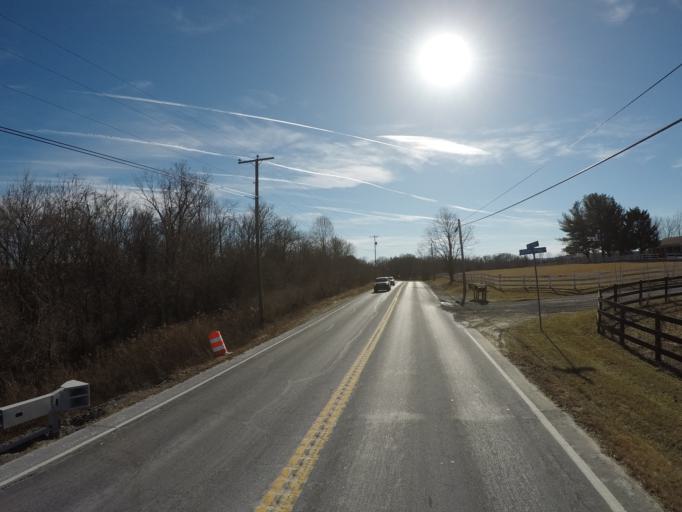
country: US
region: Maryland
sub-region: Frederick County
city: Point of Rocks
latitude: 39.2378
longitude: -77.5323
